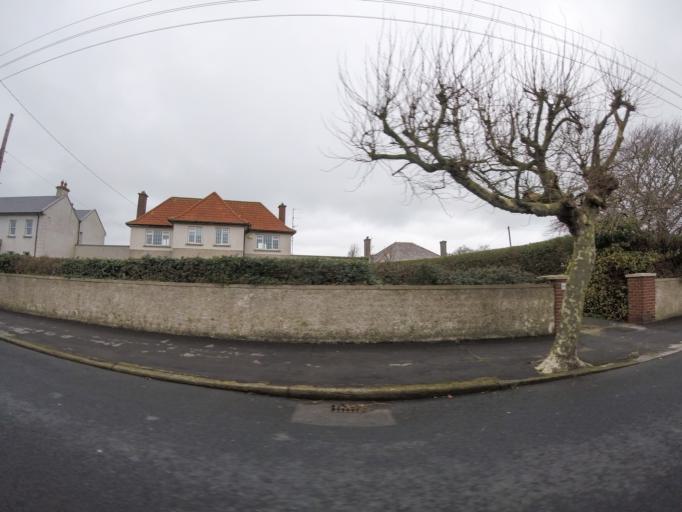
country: IE
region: Munster
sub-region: Waterford
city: Tra Mhor
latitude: 52.1590
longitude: -7.1576
